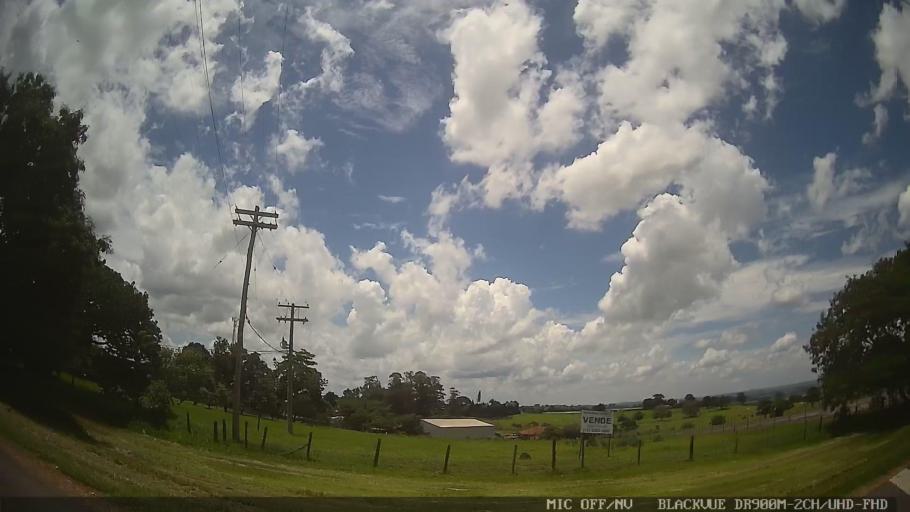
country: BR
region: Sao Paulo
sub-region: Laranjal Paulista
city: Laranjal Paulista
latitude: -23.0384
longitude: -47.8559
